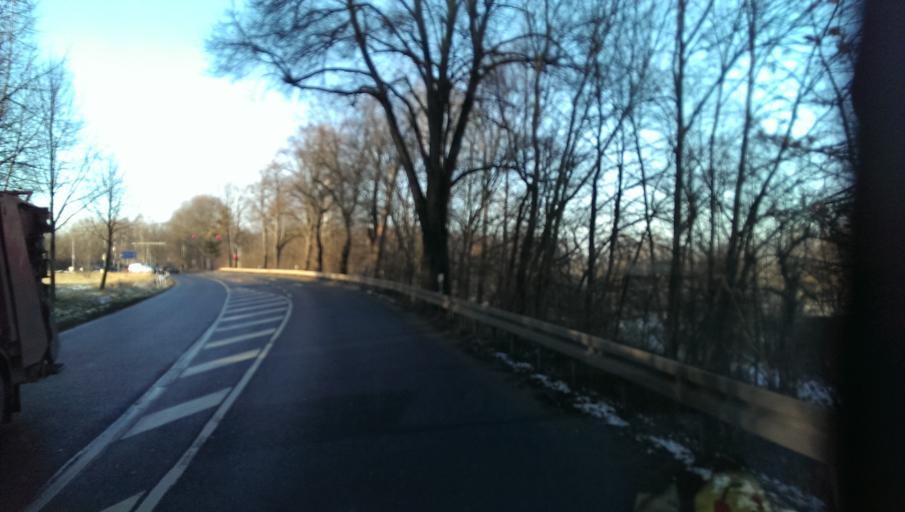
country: DE
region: Saxony
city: Wilsdruff
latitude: 51.0618
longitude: 13.5250
